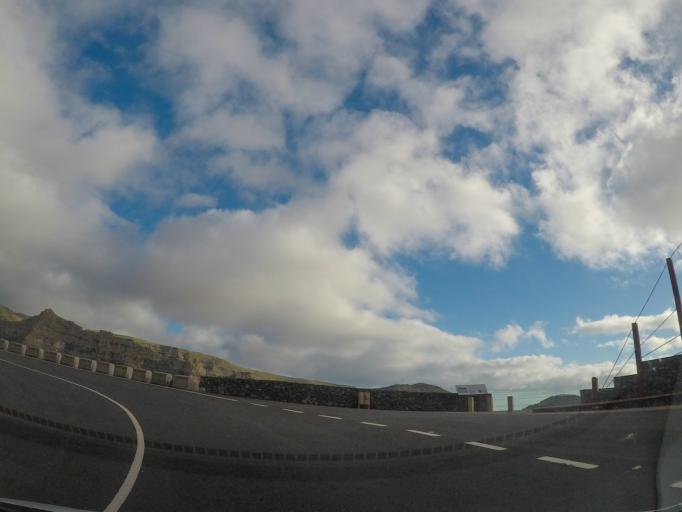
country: ES
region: Canary Islands
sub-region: Provincia de Santa Cruz de Tenerife
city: Vallehermosa
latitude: 28.1151
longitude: -17.3210
